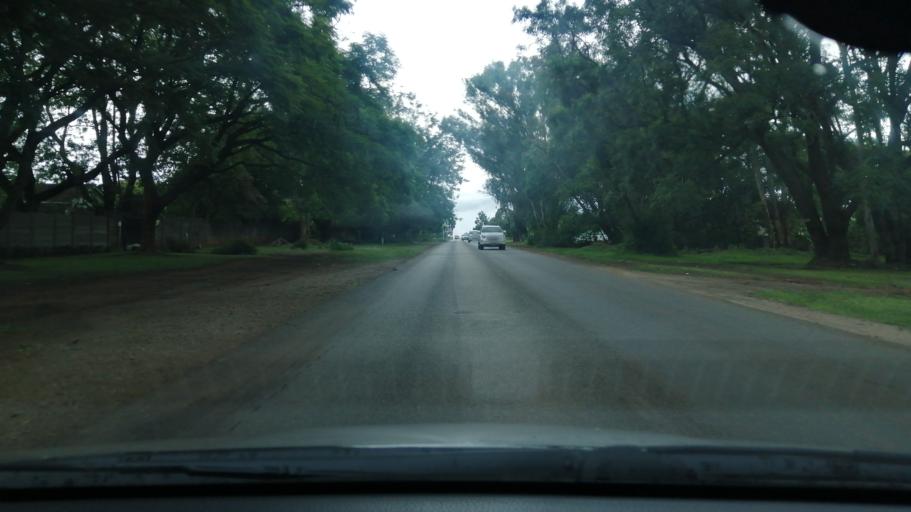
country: ZW
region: Harare
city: Harare
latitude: -17.7960
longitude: 31.0699
